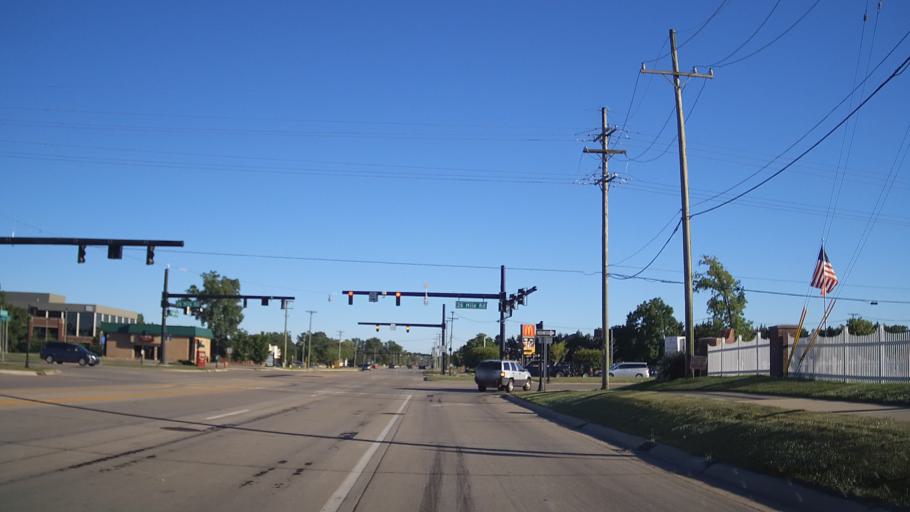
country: US
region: Michigan
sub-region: Macomb County
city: Shelby
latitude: 42.7144
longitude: -83.0354
